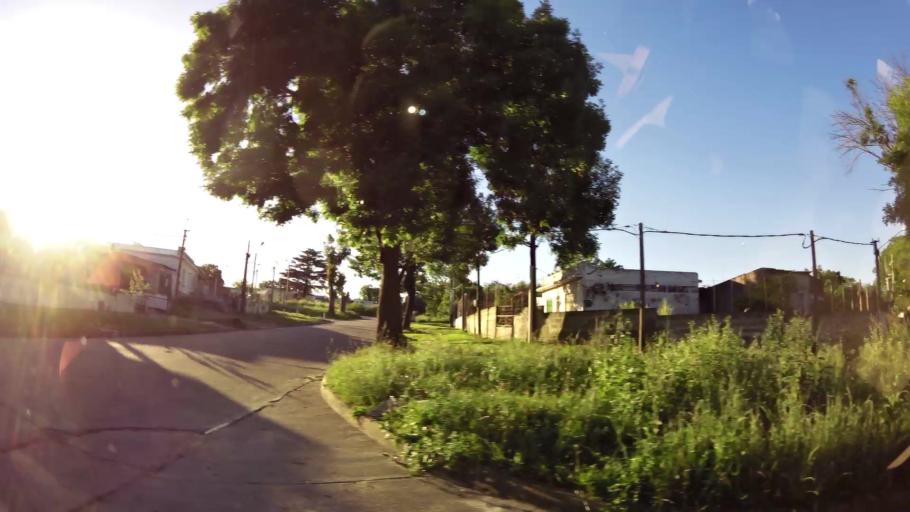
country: UY
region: Montevideo
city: Montevideo
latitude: -34.8475
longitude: -56.2159
